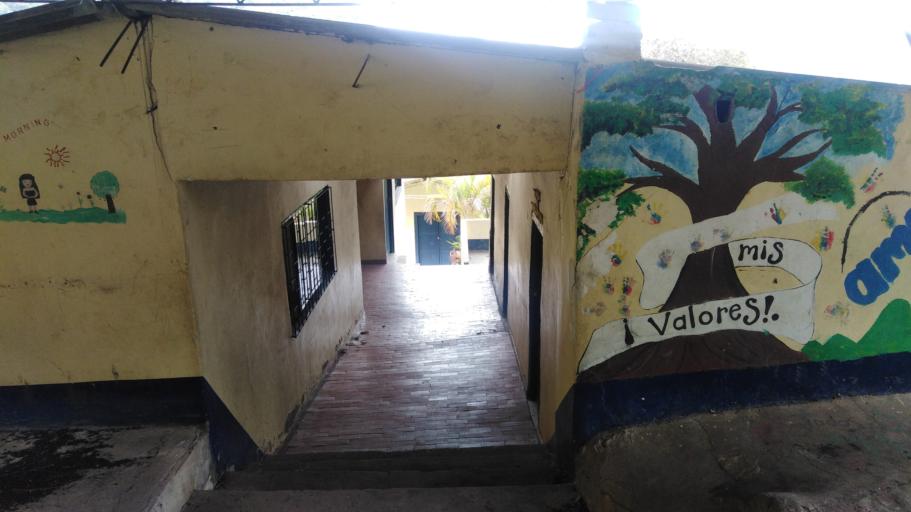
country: CO
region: Boyaca
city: San Mateo
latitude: 6.4631
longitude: -72.5638
